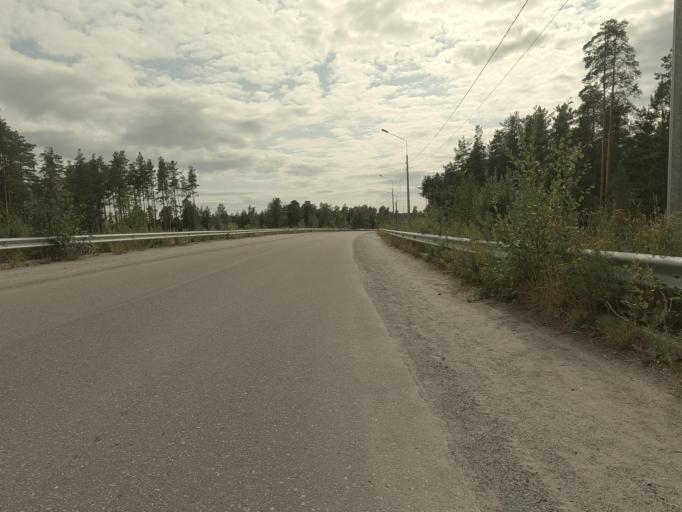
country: RU
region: Leningrad
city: Kamennogorsk
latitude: 60.9586
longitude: 29.1382
